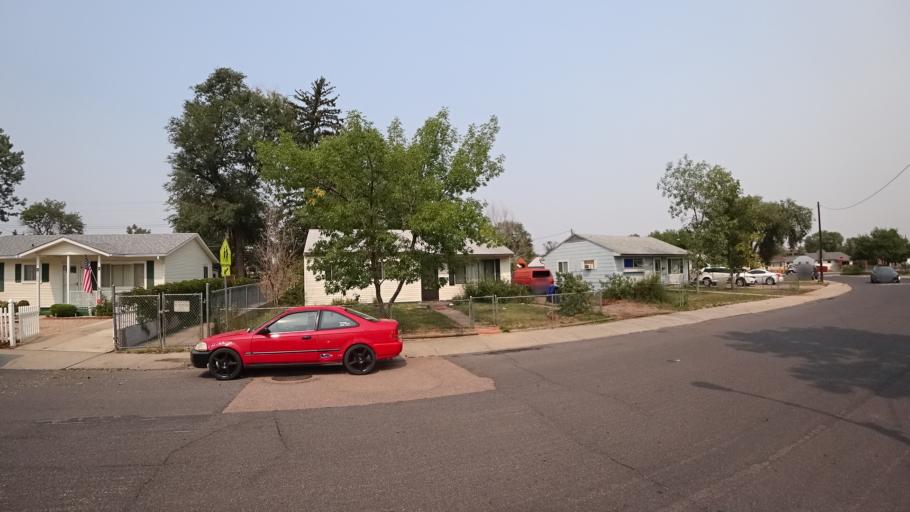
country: US
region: Colorado
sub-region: El Paso County
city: Colorado Springs
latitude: 38.8003
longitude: -104.8066
